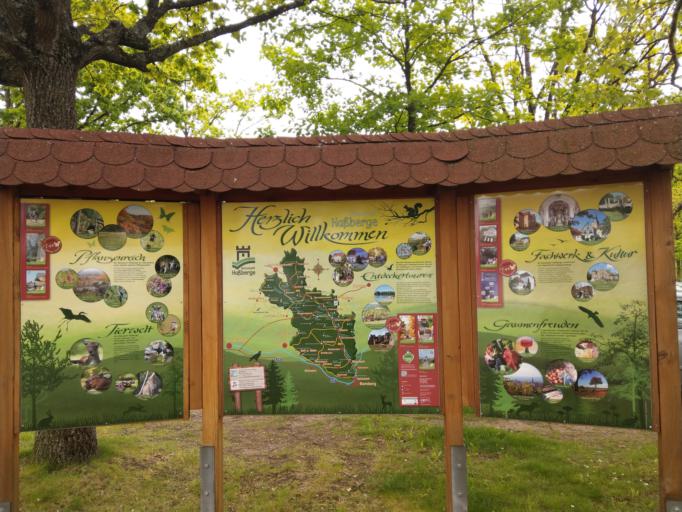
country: DE
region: Bavaria
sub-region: Regierungsbezirk Unterfranken
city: Hassfurt
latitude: 50.0306
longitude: 10.5026
